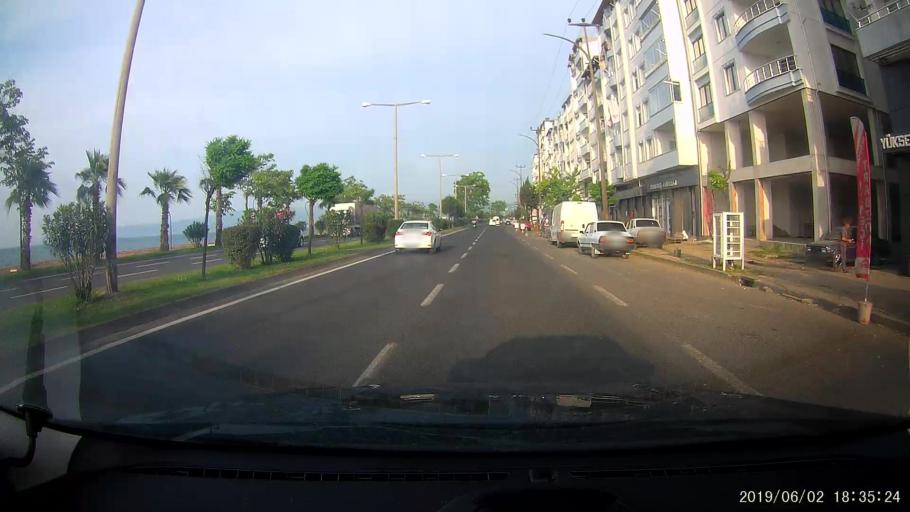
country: TR
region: Ordu
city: Fatsa
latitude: 41.0265
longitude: 37.5155
